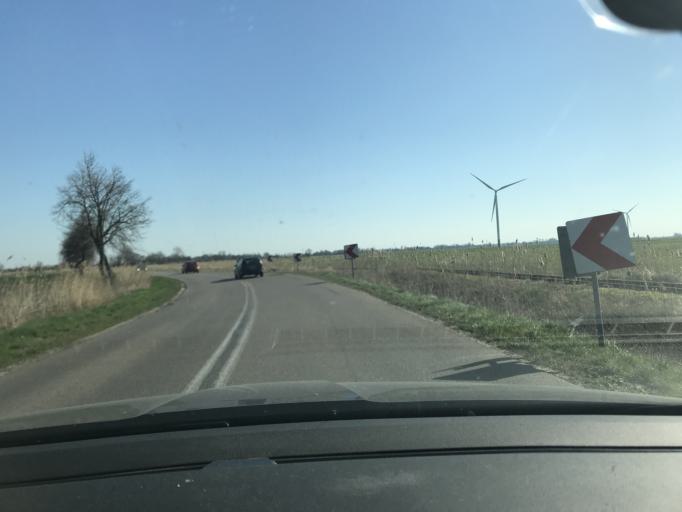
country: PL
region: Pomeranian Voivodeship
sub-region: Powiat nowodworski
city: Nowy Dwor Gdanski
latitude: 54.2586
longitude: 19.1366
